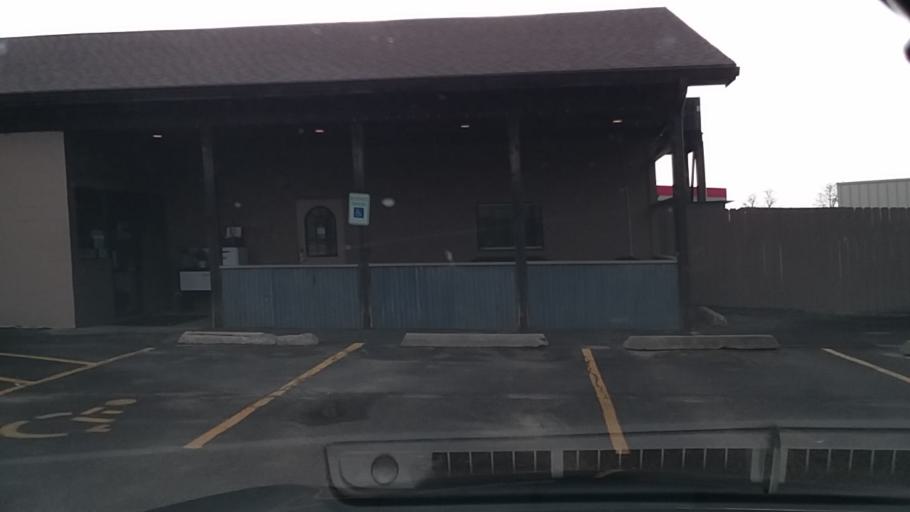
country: US
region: Kansas
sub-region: Douglas County
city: Baldwin City
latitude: 38.7826
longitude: -95.1852
